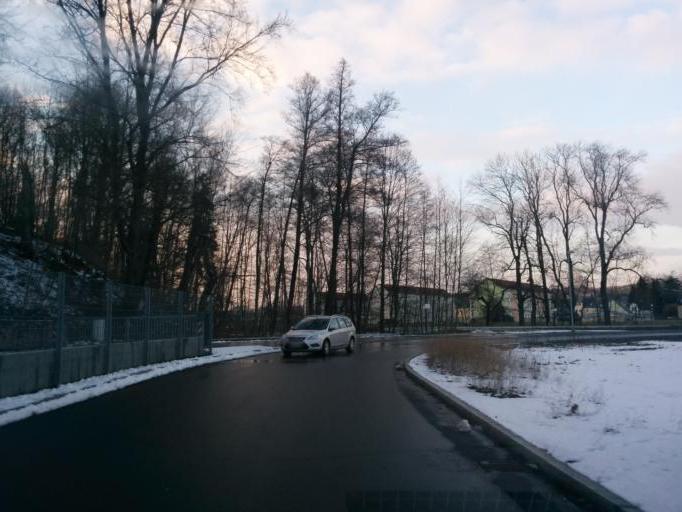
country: DE
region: Saxony
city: Floha
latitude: 50.8526
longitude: 13.0704
